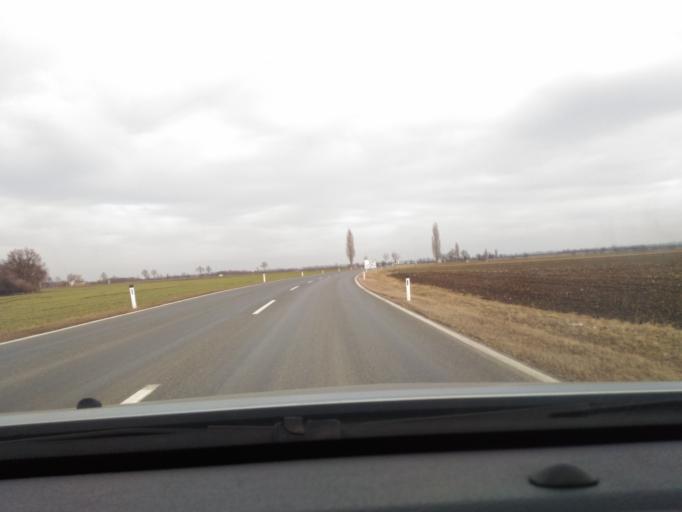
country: AT
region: Lower Austria
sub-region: Politischer Bezirk Hollabrunn
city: Mailberg
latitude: 48.7031
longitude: 16.1847
